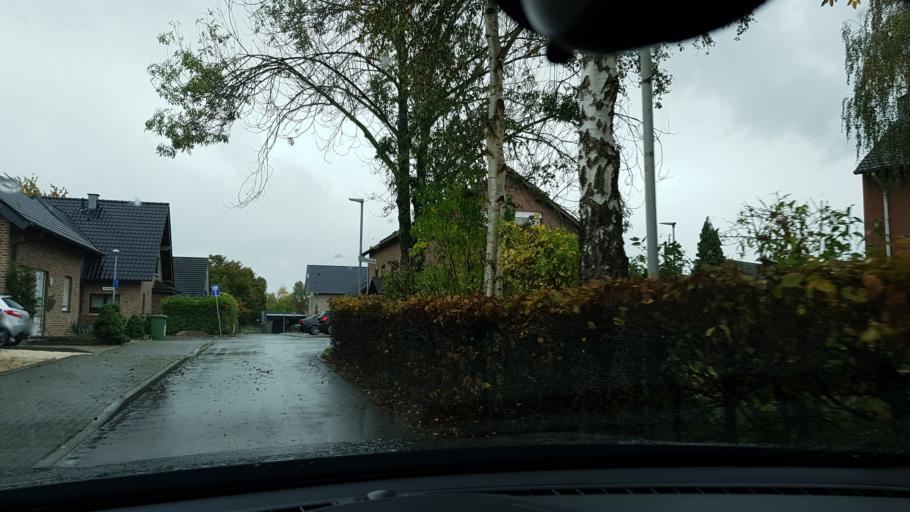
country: DE
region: North Rhine-Westphalia
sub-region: Regierungsbezirk Dusseldorf
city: Rommerskirchen
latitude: 51.0741
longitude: 6.6894
